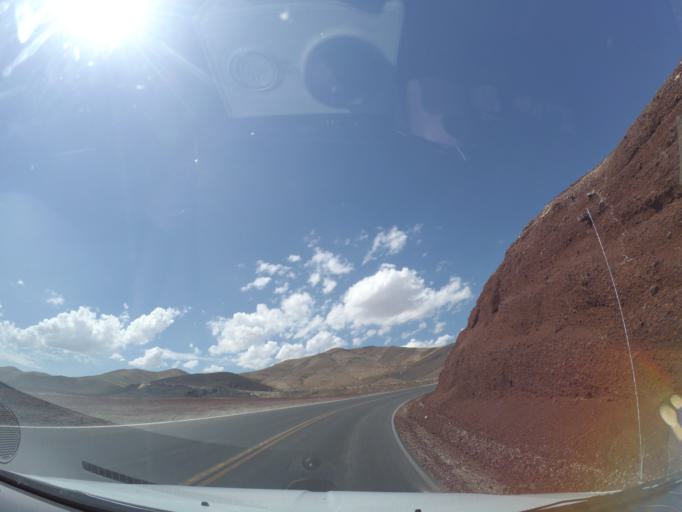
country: US
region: California
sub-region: Inyo County
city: Lone Pine
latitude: 36.3576
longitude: -117.5309
